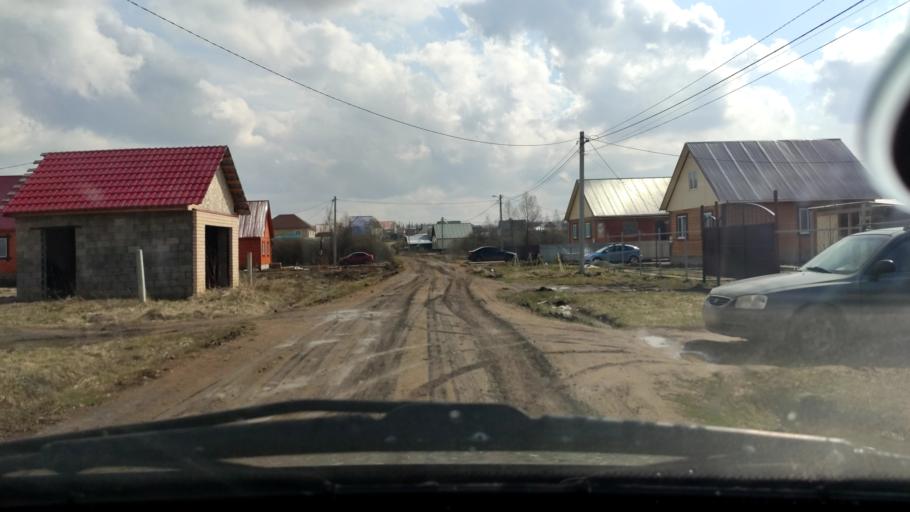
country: RU
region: Bashkortostan
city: Iglino
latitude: 54.8244
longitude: 56.3714
